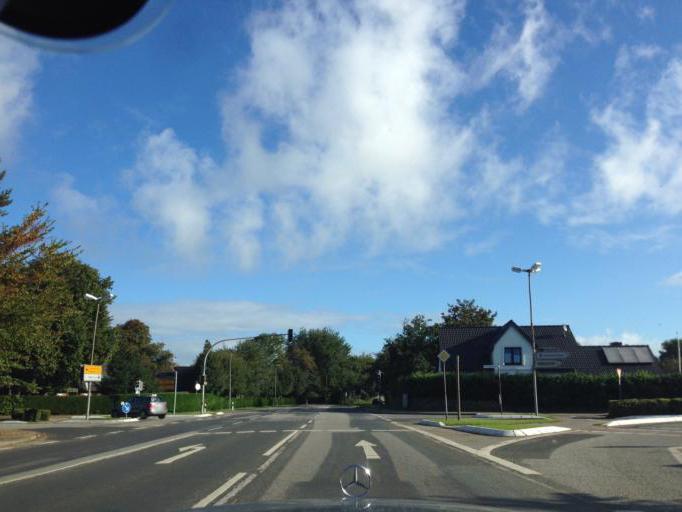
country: DE
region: Schleswig-Holstein
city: Wrixum
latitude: 54.6948
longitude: 8.5570
